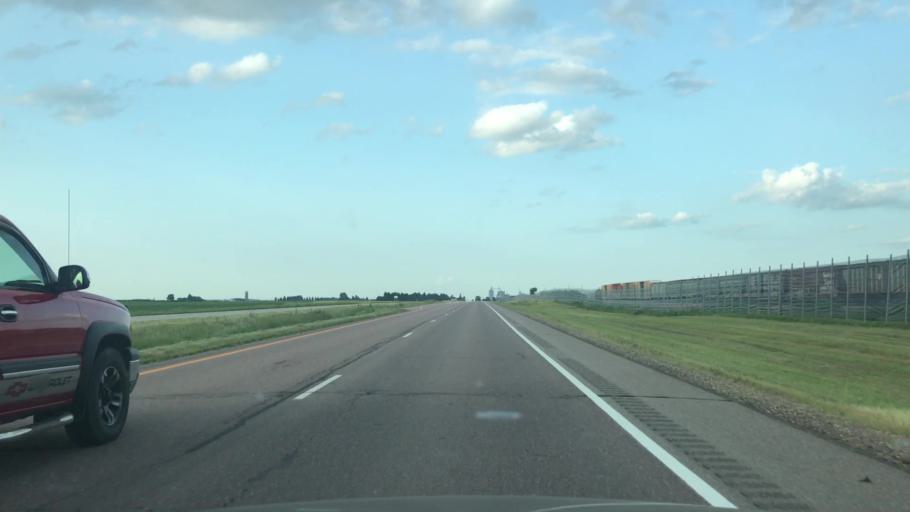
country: US
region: Minnesota
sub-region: Nobles County
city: Worthington
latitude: 43.6742
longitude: -95.5090
